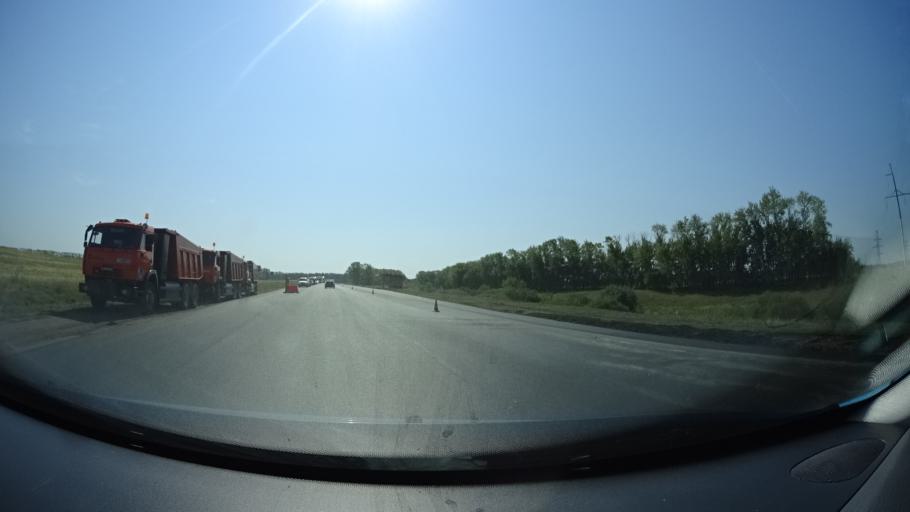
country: RU
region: Bashkortostan
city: Kabakovo
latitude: 54.4863
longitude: 55.9203
